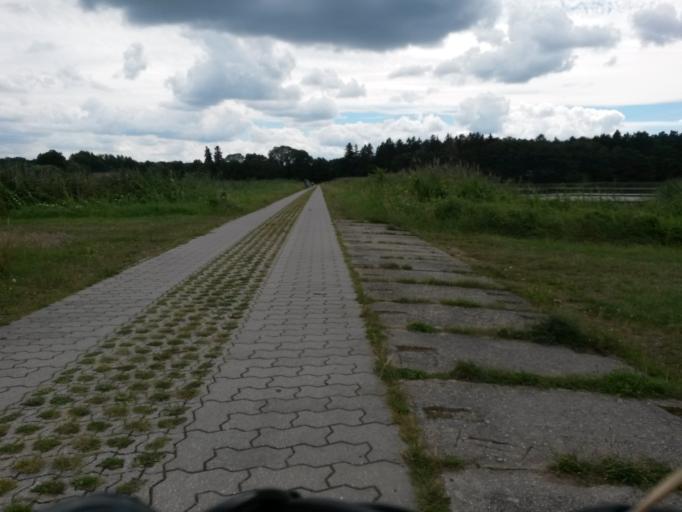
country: DE
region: Brandenburg
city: Angermunde
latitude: 53.0412
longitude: 13.9426
